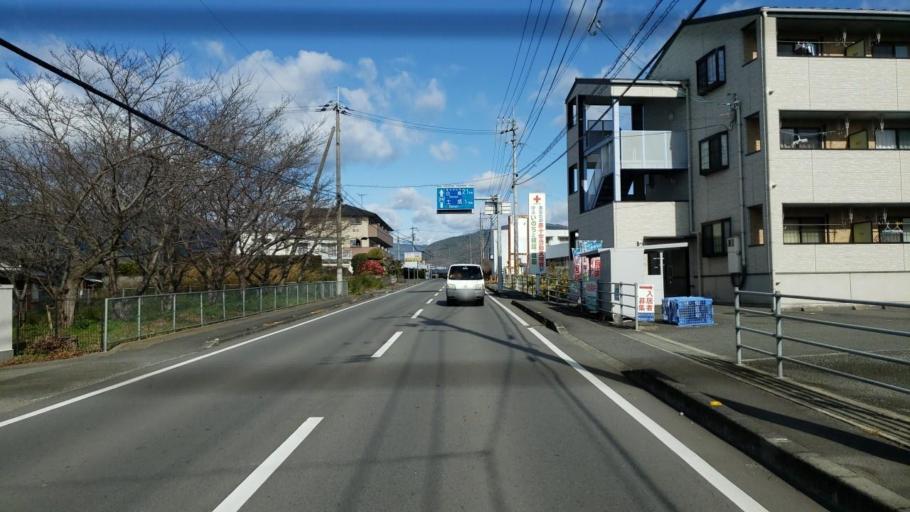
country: JP
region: Tokushima
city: Kamojimacho-jogejima
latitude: 34.0969
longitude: 134.3444
